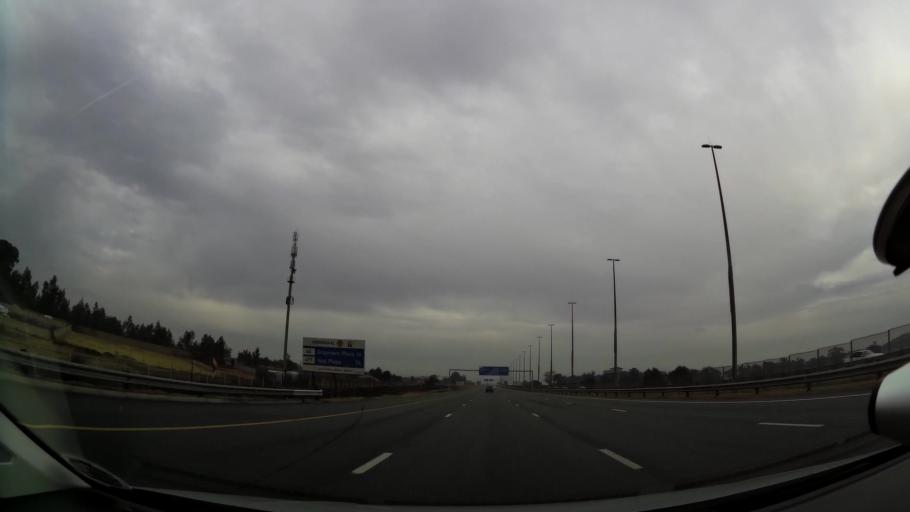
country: ZA
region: Gauteng
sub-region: City of Johannesburg Metropolitan Municipality
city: Soweto
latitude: -26.2886
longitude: 27.9468
